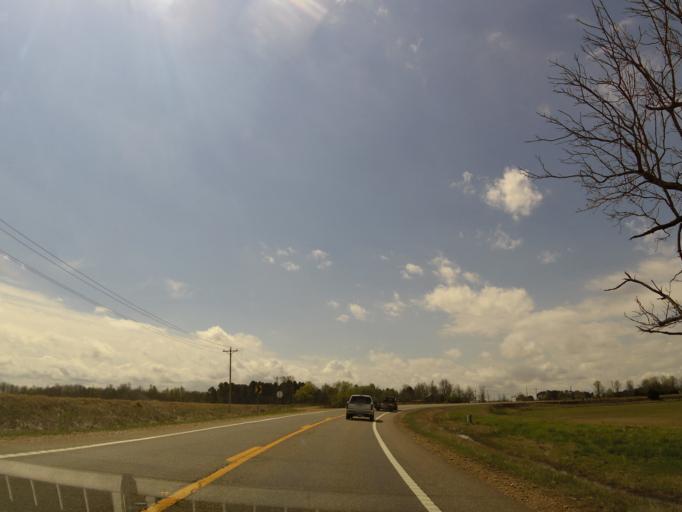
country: US
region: Arkansas
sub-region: Clay County
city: Corning
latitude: 36.3886
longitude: -90.5152
